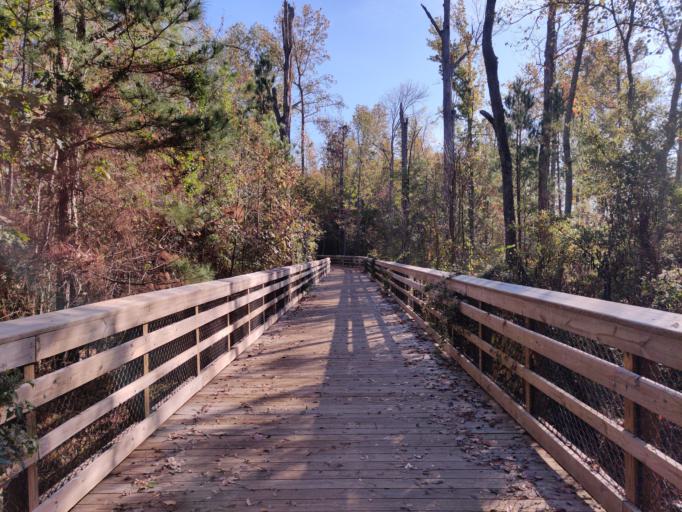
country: US
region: North Carolina
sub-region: Wake County
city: Morrisville
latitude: 35.8167
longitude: -78.8323
